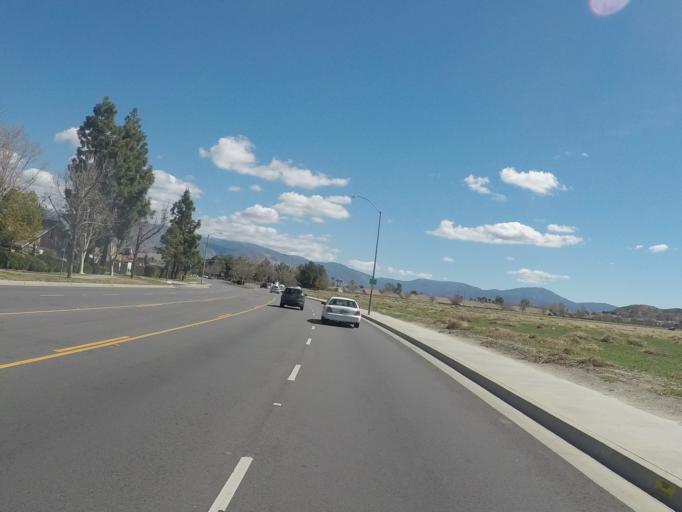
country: US
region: California
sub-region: Riverside County
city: San Jacinto
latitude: 33.7725
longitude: -116.9535
